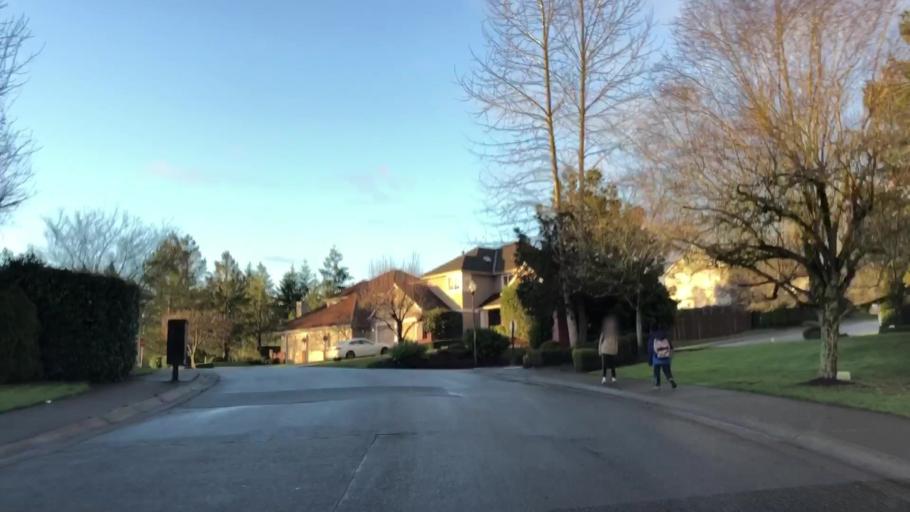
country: US
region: Washington
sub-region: King County
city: City of Sammamish
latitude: 47.6227
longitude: -122.0269
